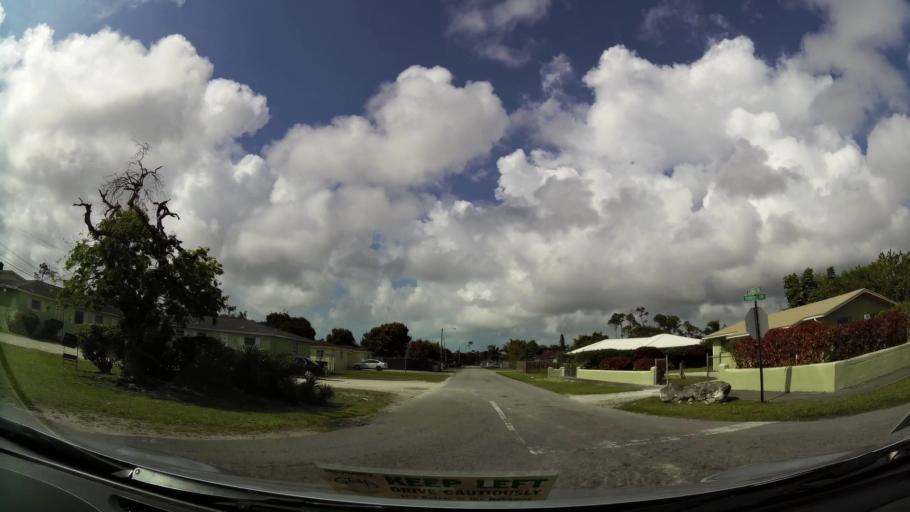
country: BS
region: Freeport
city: Lucaya
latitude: 26.5293
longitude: -78.6809
